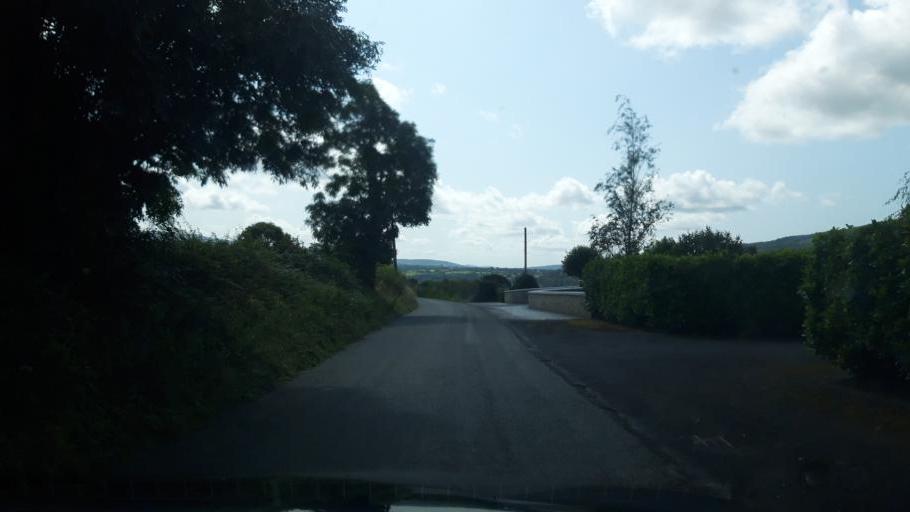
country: IE
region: Leinster
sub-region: Kilkenny
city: Graiguenamanagh
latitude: 52.5503
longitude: -6.9714
